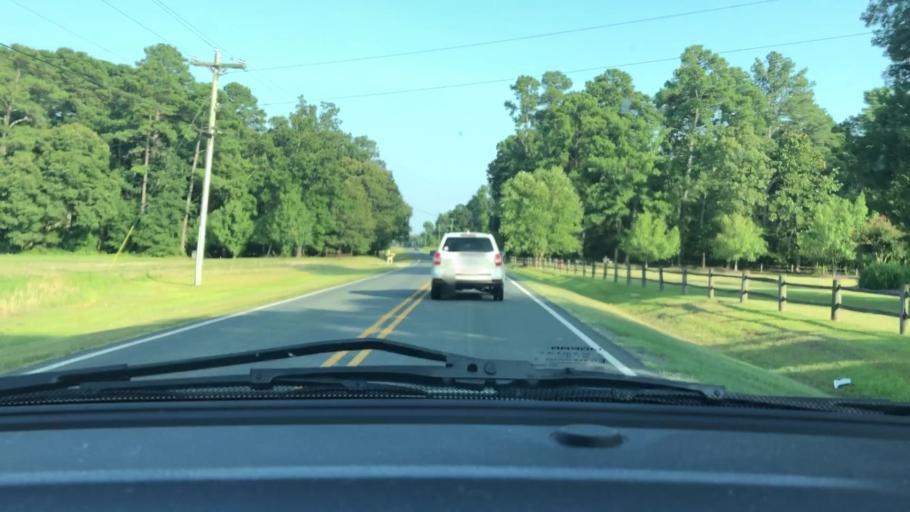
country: US
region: North Carolina
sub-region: Lee County
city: Broadway
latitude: 35.3543
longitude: -79.0767
